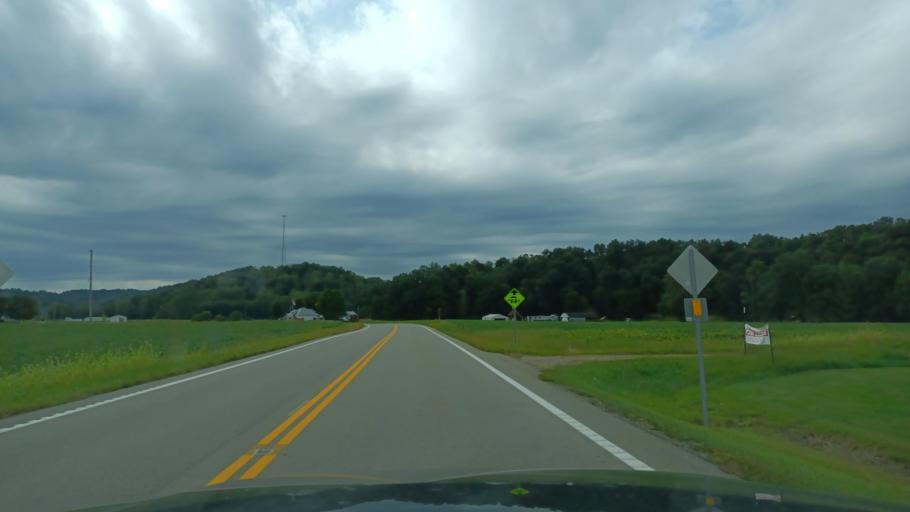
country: US
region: Ohio
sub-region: Vinton County
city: McArthur
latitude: 39.2727
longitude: -82.6571
